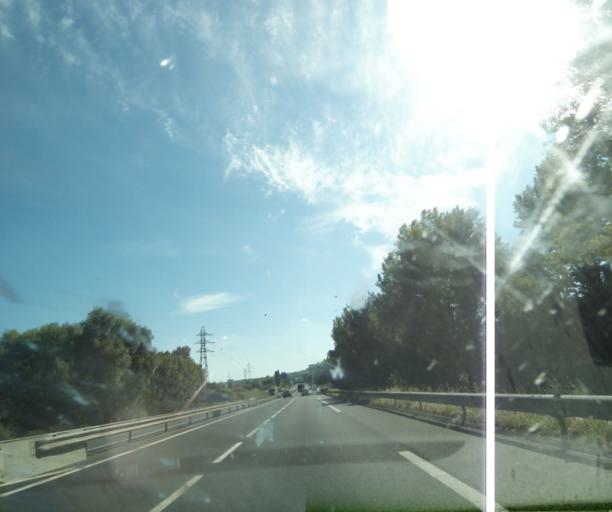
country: FR
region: Limousin
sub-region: Departement de la Correze
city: Saint-Pantaleon-de-Larche
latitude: 45.1524
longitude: 1.4838
